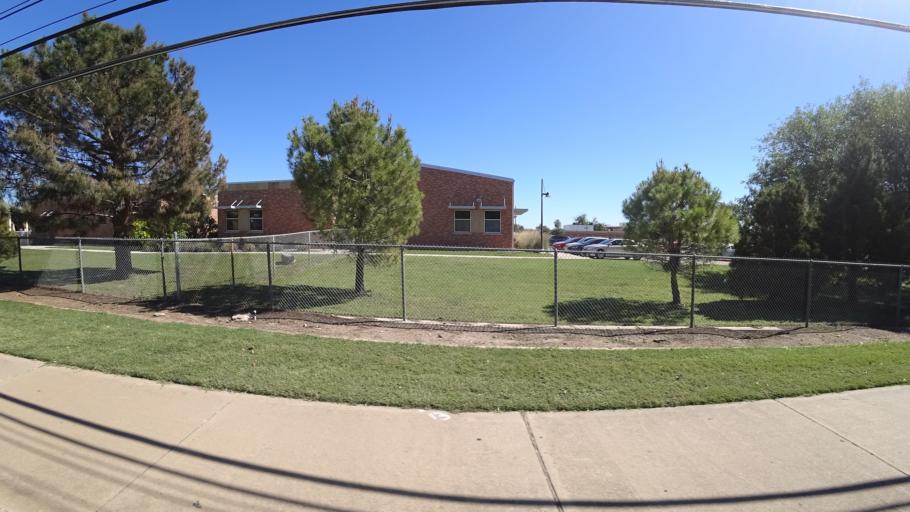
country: US
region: Texas
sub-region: Travis County
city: Austin
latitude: 30.3163
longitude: -97.7409
